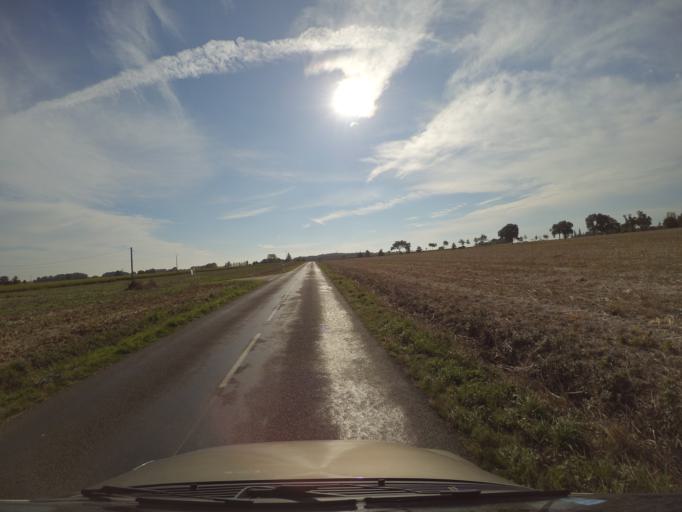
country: FR
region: Pays de la Loire
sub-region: Departement de Maine-et-Loire
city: Saint-Crespin-sur-Moine
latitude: 47.1231
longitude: -1.2220
